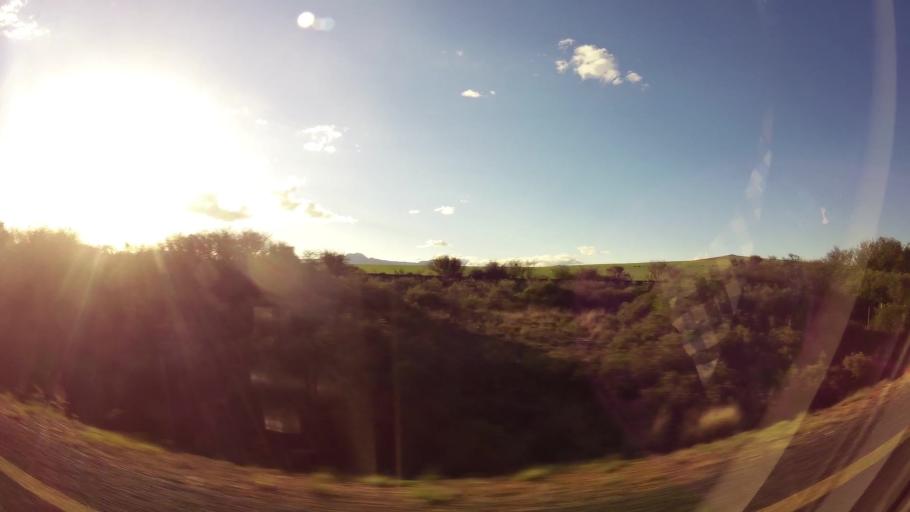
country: ZA
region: Western Cape
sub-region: Eden District Municipality
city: Riversdale
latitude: -34.0862
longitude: 20.9834
